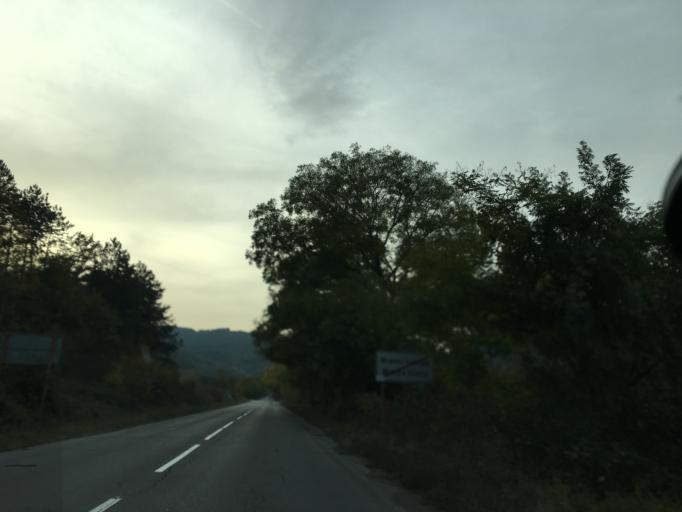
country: BG
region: Pazardzhik
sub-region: Obshtina Belovo
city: Belovo
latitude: 42.2302
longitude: 23.9640
